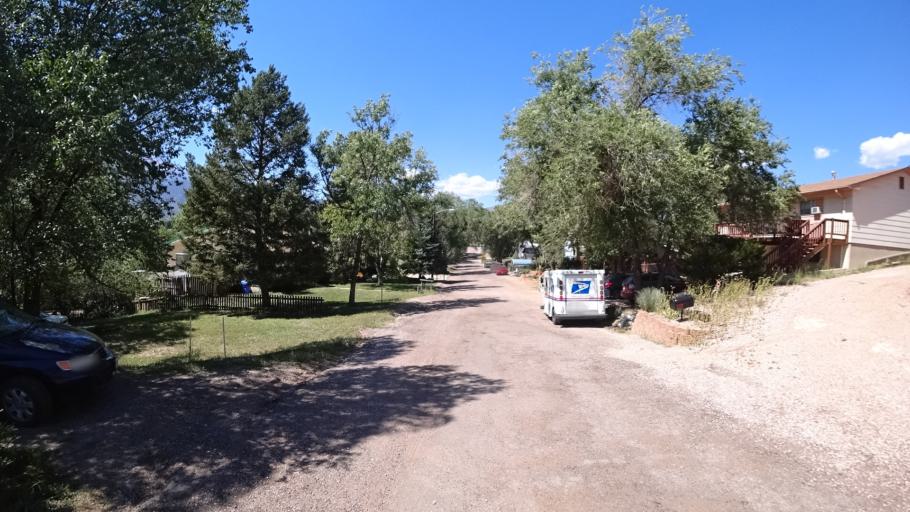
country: US
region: Colorado
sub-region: El Paso County
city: Manitou Springs
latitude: 38.8586
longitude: -104.8729
